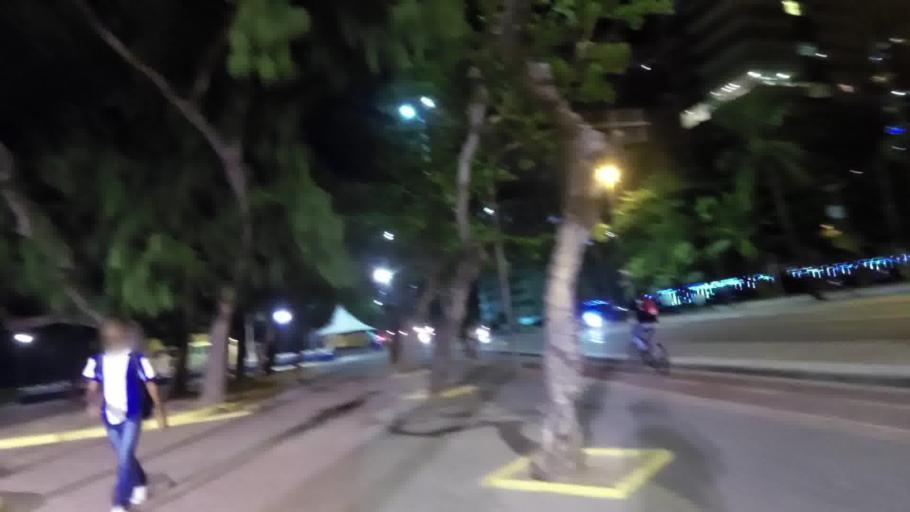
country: BR
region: Pernambuco
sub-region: Recife
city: Recife
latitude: -8.1018
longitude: -34.8853
